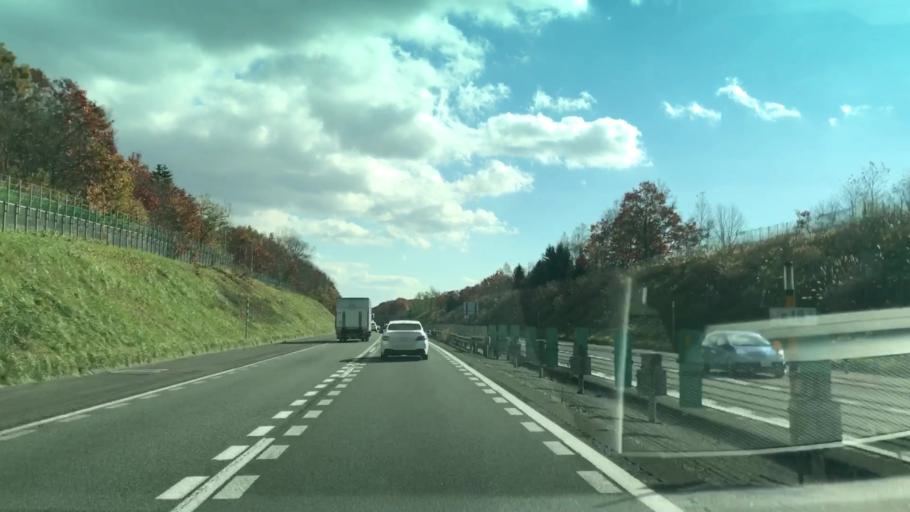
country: JP
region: Hokkaido
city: Kitahiroshima
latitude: 42.9364
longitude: 141.5253
